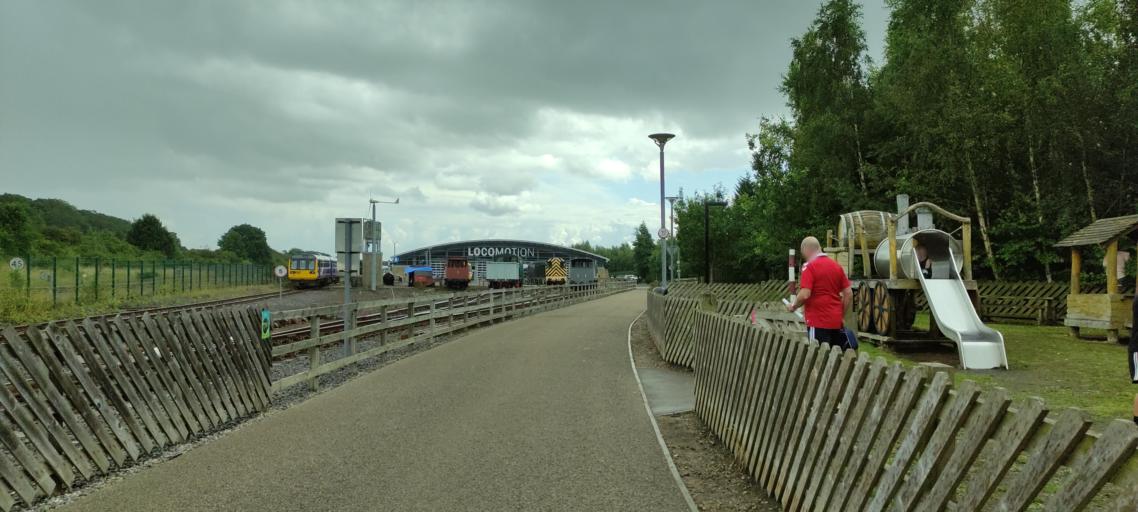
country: GB
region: England
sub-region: County Durham
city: Shildon
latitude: 54.6252
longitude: -1.6333
